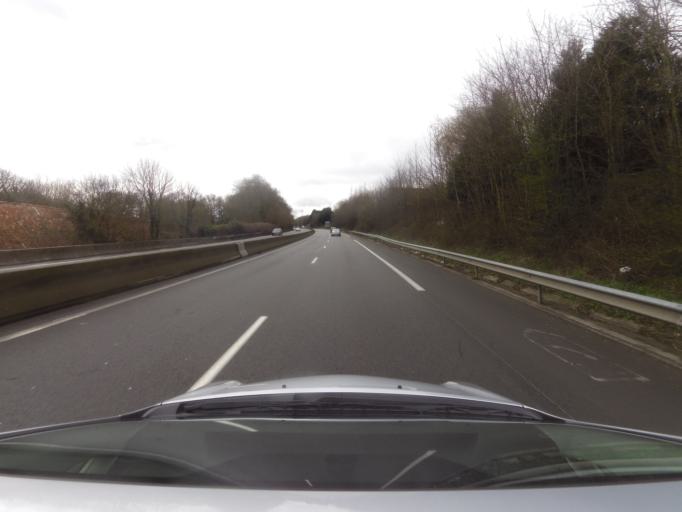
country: FR
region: Nord-Pas-de-Calais
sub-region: Departement du Pas-de-Calais
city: Wimille
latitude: 50.7614
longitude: 1.6344
